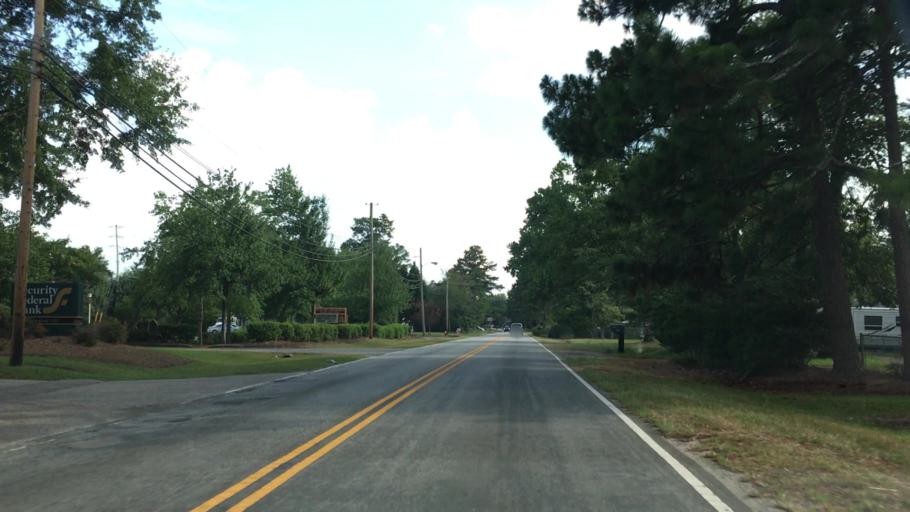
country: US
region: South Carolina
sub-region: Aiken County
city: Aiken
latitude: 33.5292
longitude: -81.7245
